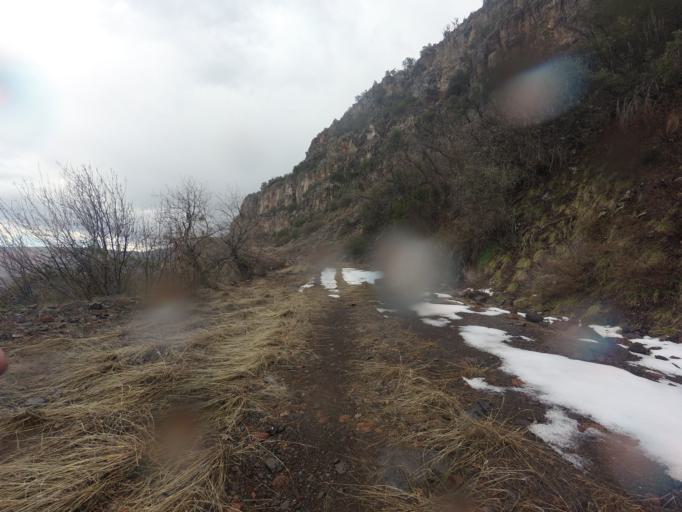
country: US
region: Arizona
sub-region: Gila County
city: Pine
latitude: 34.4082
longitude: -111.5838
